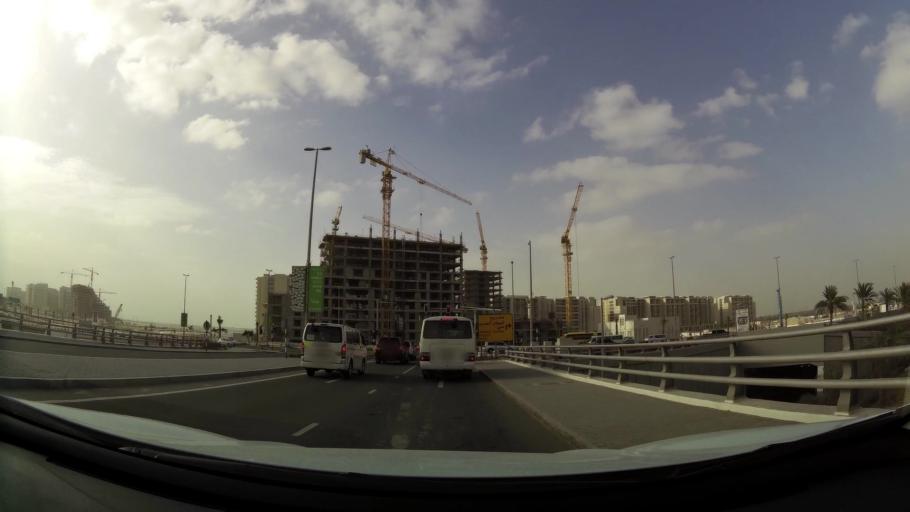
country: AE
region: Abu Dhabi
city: Abu Dhabi
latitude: 24.4510
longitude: 54.6151
